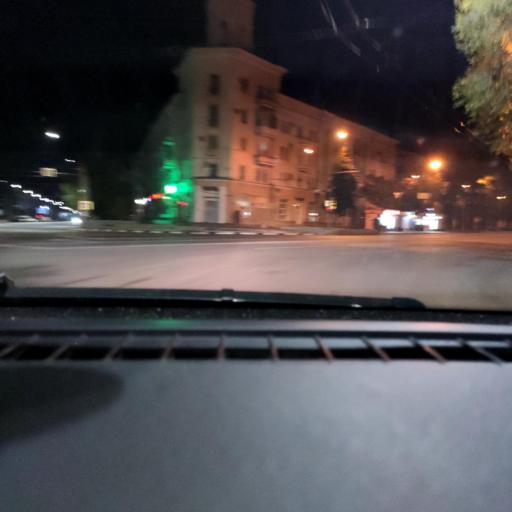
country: RU
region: Voronezj
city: Voronezh
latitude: 51.6331
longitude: 39.2325
